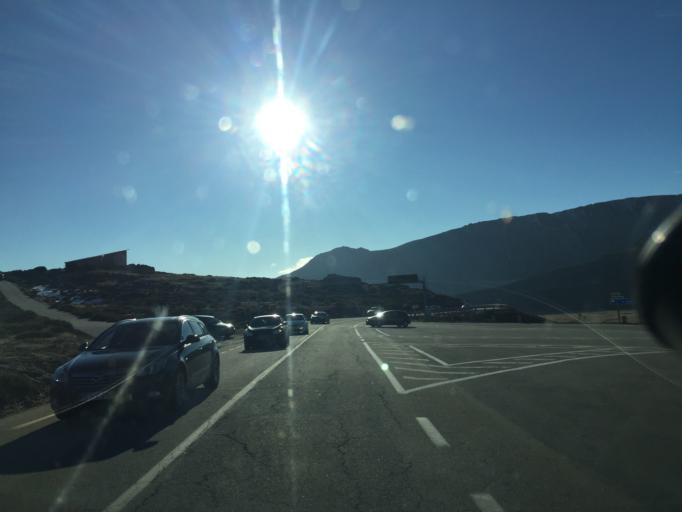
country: PT
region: Castelo Branco
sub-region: Covilha
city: Covilha
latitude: 40.3168
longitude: -7.5740
